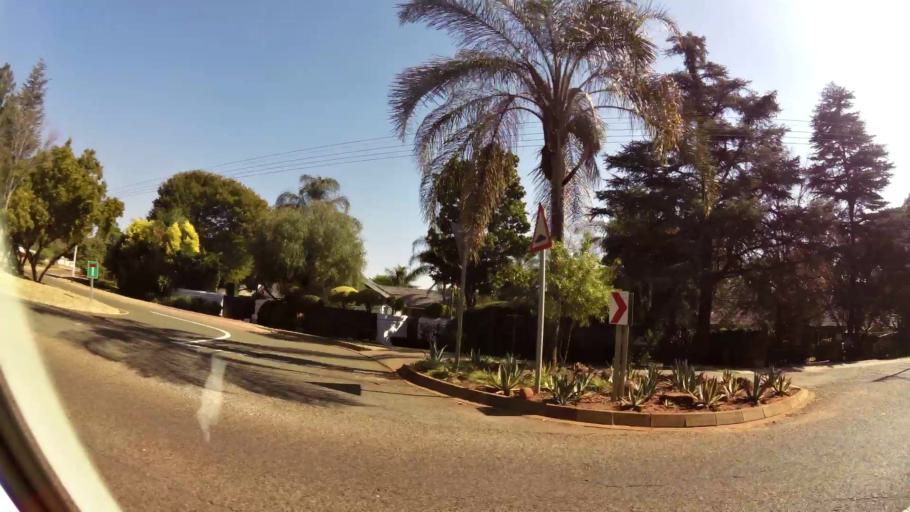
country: ZA
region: Gauteng
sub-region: City of Tshwane Metropolitan Municipality
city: Pretoria
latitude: -25.7587
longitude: 28.2653
